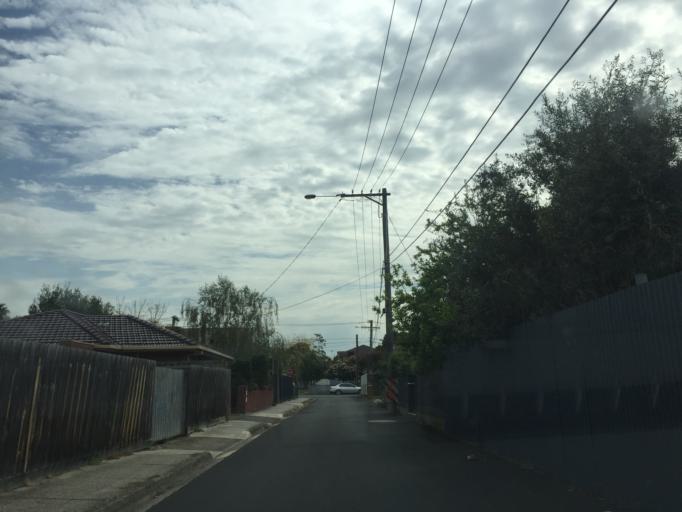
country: AU
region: Victoria
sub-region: Darebin
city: Preston
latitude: -37.7443
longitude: 145.0170
